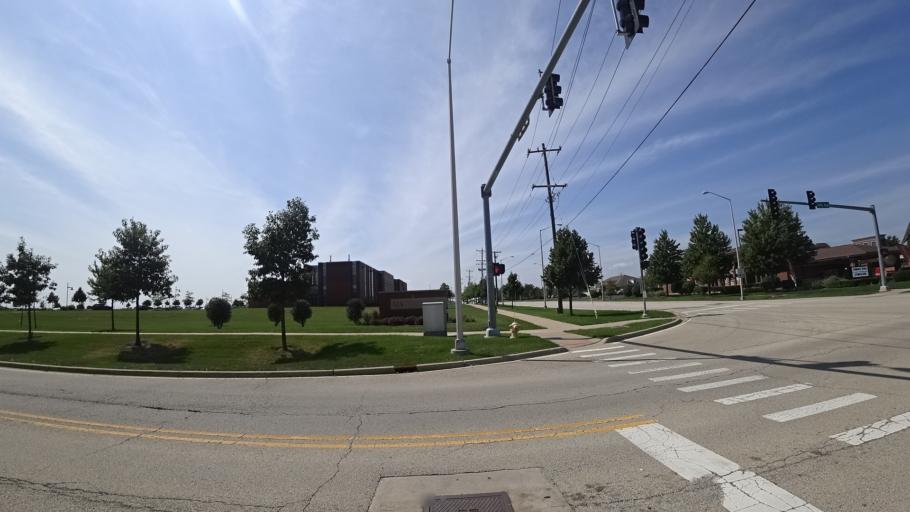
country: US
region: Illinois
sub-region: Cook County
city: Orland Hills
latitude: 41.5648
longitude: -87.8466
